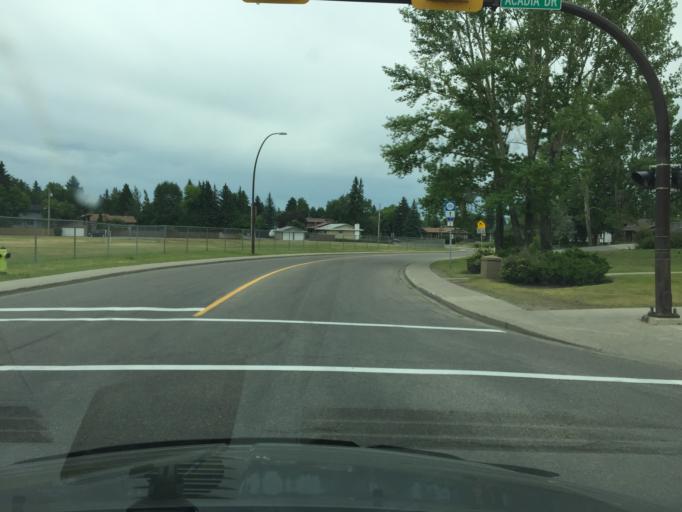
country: CA
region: Alberta
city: Calgary
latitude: 50.9421
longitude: -114.0446
